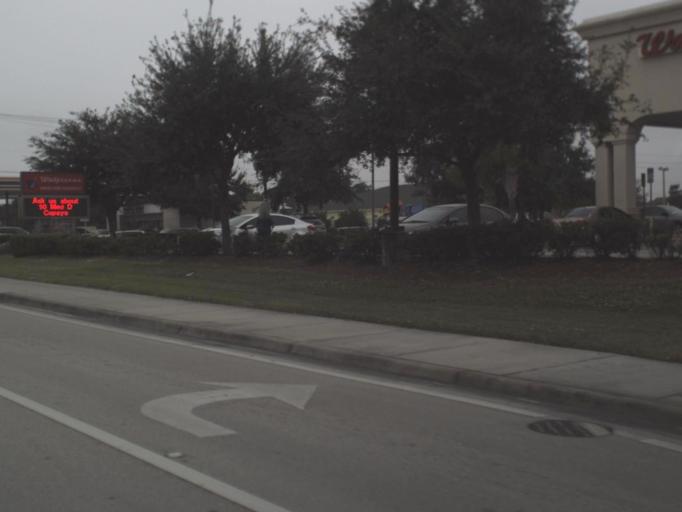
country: US
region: Florida
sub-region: Brevard County
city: West Melbourne
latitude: 28.0354
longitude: -80.6375
